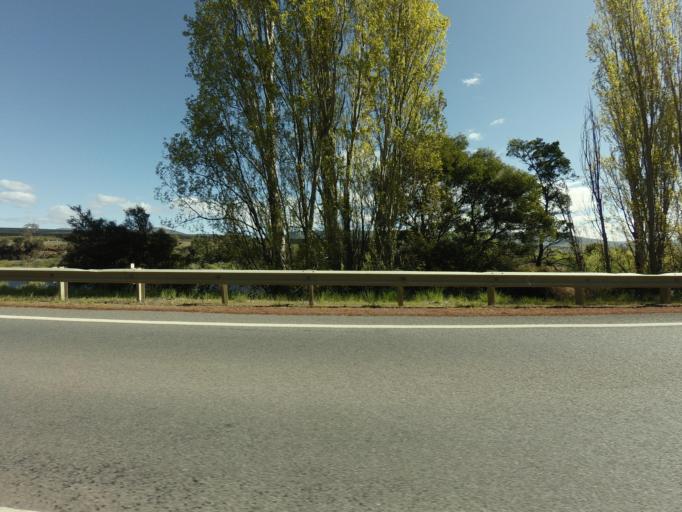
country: AU
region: Tasmania
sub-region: Derwent Valley
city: New Norfolk
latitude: -42.7369
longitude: 146.9773
